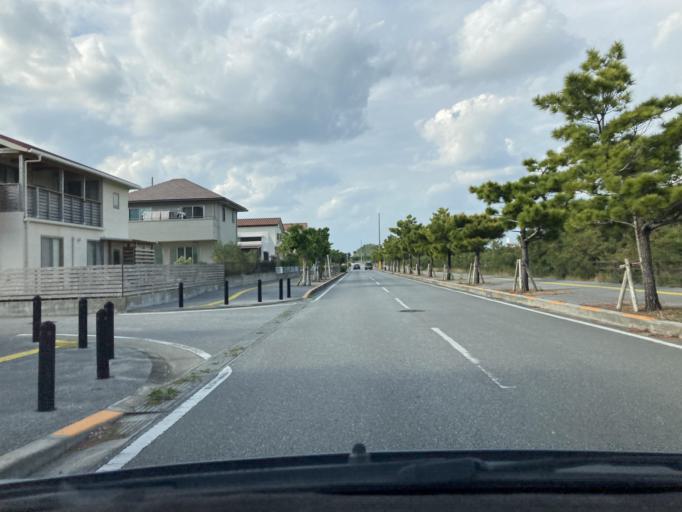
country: JP
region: Okinawa
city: Itoman
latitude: 26.1553
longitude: 127.6665
